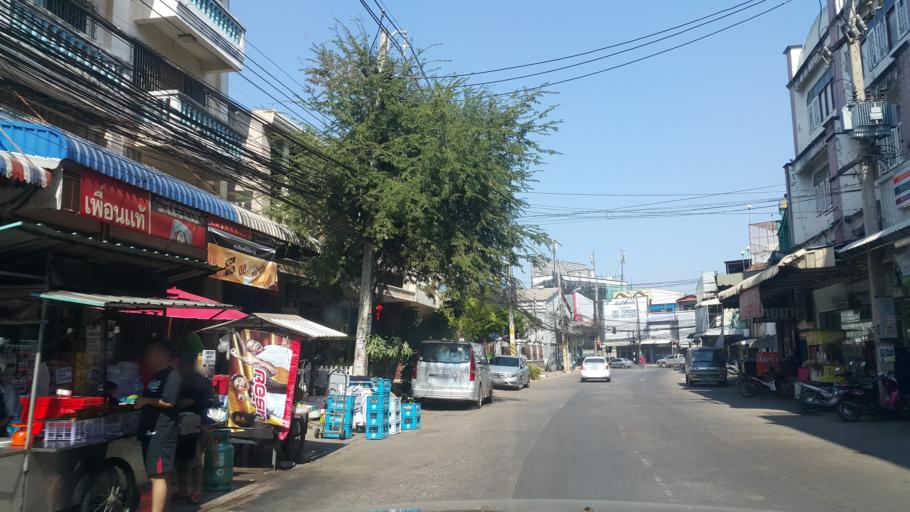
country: TH
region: Changwat Udon Thani
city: Udon Thani
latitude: 17.3951
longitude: 102.8091
